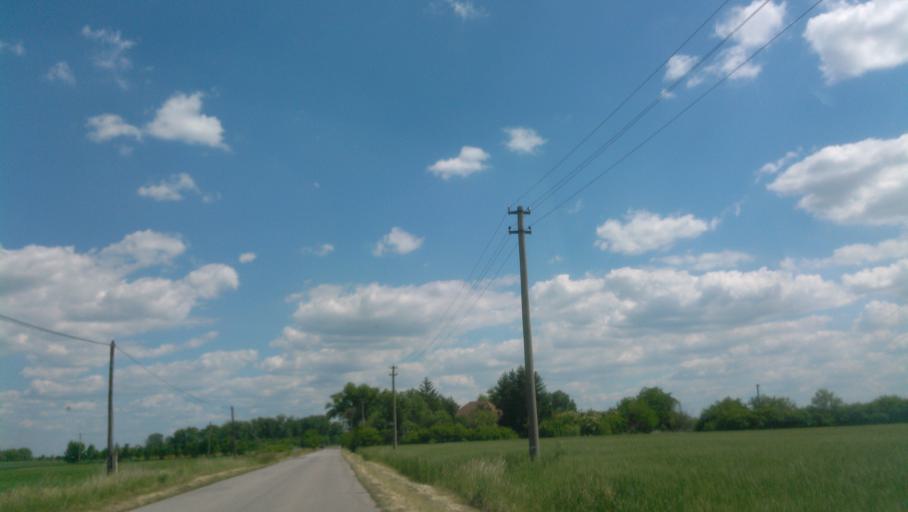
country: SK
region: Nitriansky
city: Kolarovo
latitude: 47.8846
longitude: 17.9032
